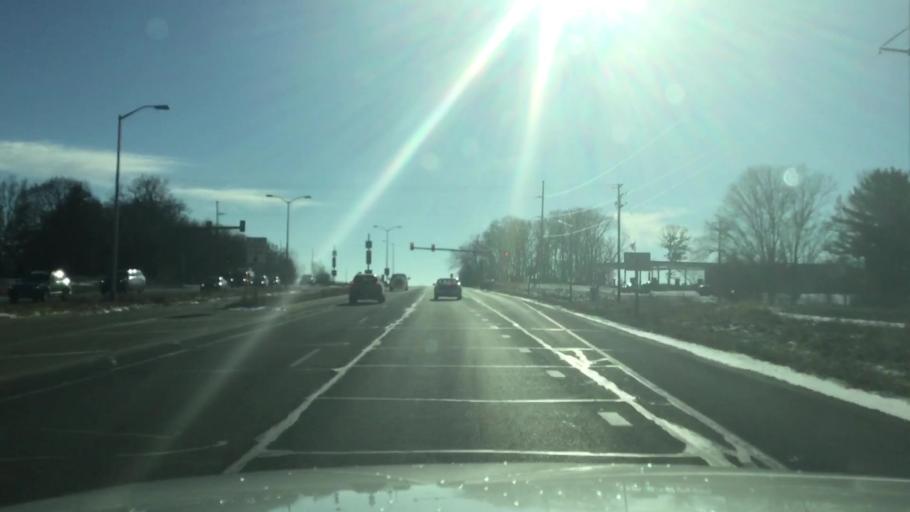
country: US
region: Wisconsin
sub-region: Racine County
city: Rochester
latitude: 42.7425
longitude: -88.2154
